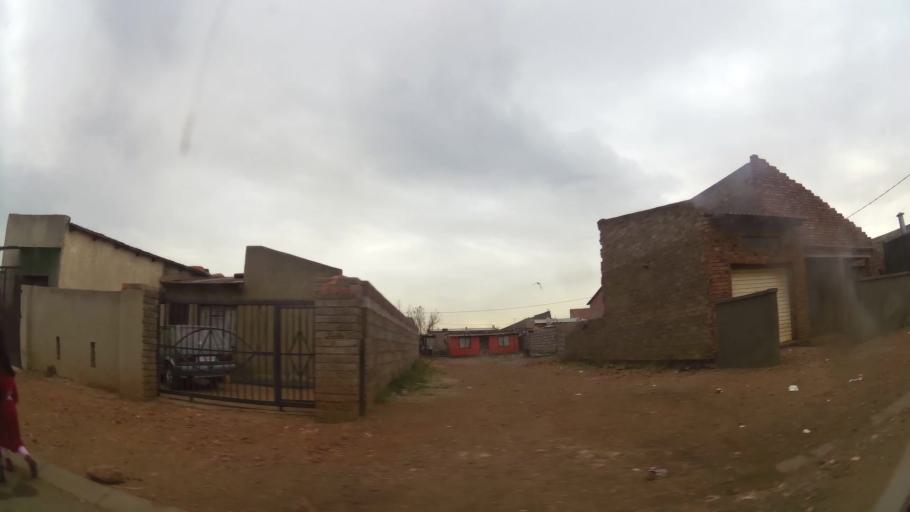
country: ZA
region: Gauteng
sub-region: Ekurhuleni Metropolitan Municipality
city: Germiston
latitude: -26.3865
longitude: 28.1749
